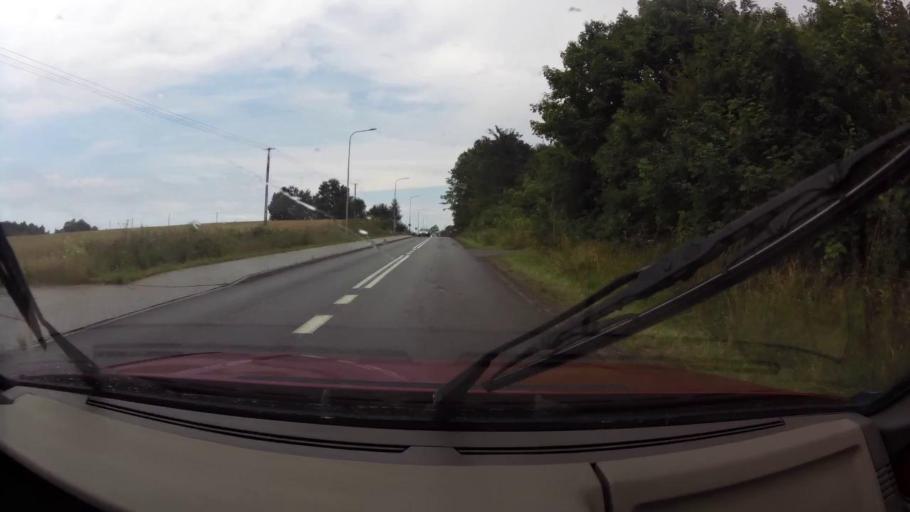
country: PL
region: West Pomeranian Voivodeship
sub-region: Koszalin
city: Koszalin
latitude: 54.1694
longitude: 16.1556
